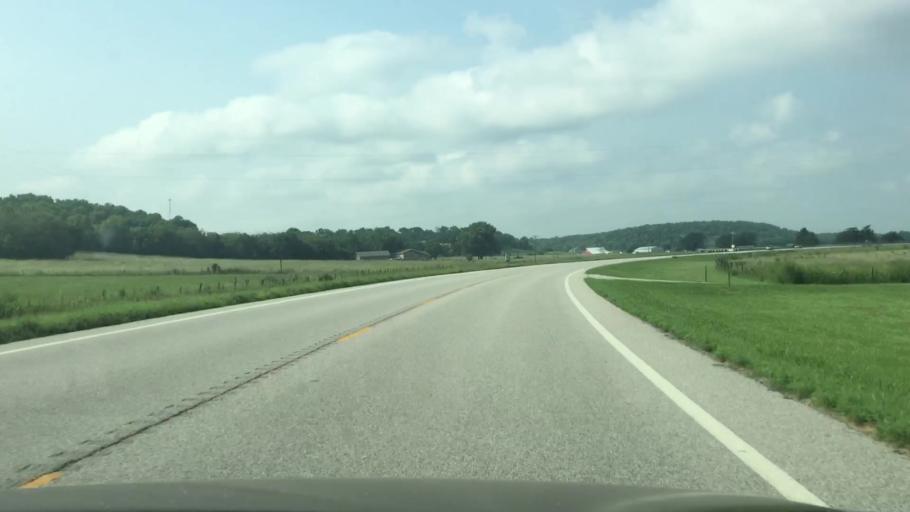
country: US
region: Kansas
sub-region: Anderson County
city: Garnett
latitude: 38.3644
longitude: -95.1193
